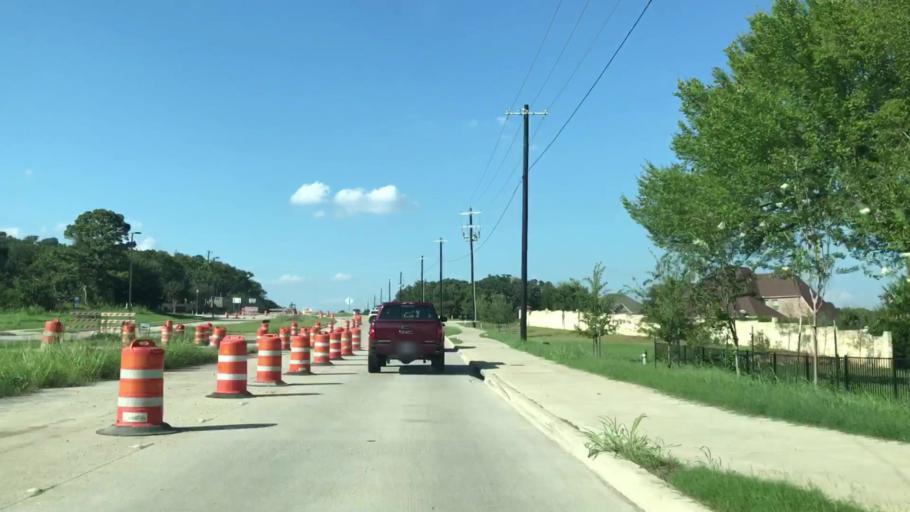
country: US
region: Texas
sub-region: Denton County
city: Trophy Club
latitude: 32.9516
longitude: -97.1856
